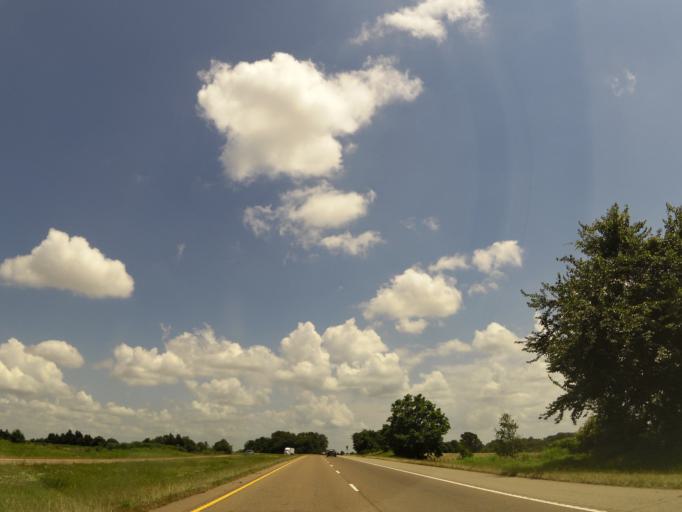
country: US
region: Tennessee
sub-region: Crockett County
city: Alamo
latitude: 35.7696
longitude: -89.1214
